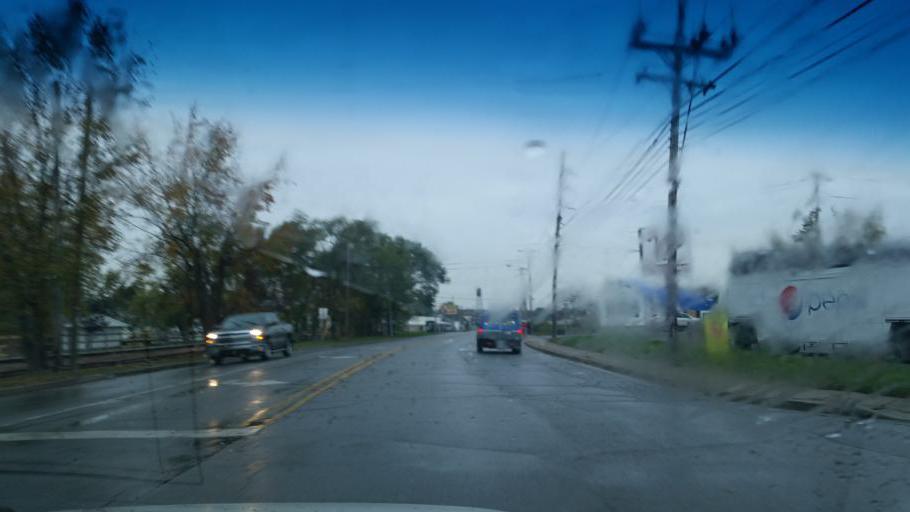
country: US
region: Indiana
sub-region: Howard County
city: Kokomo
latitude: 40.4661
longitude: -86.1239
